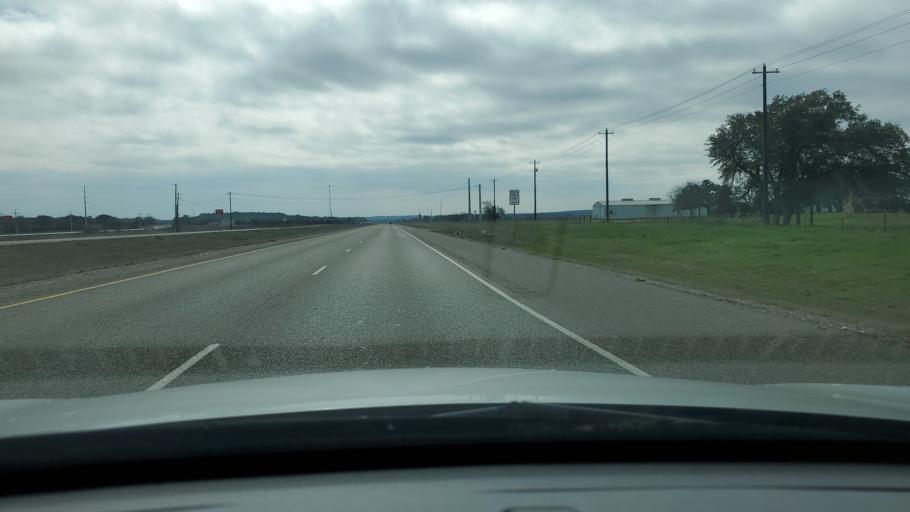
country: US
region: Texas
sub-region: Williamson County
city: Florence
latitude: 30.7885
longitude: -97.7651
